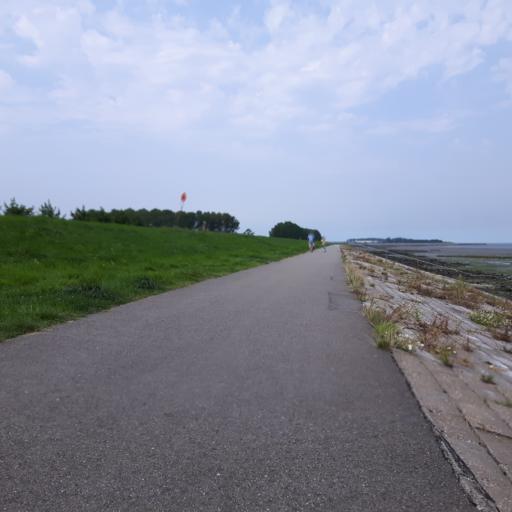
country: NL
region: Zeeland
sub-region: Gemeente Goes
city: Goes
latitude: 51.5254
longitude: 3.9403
